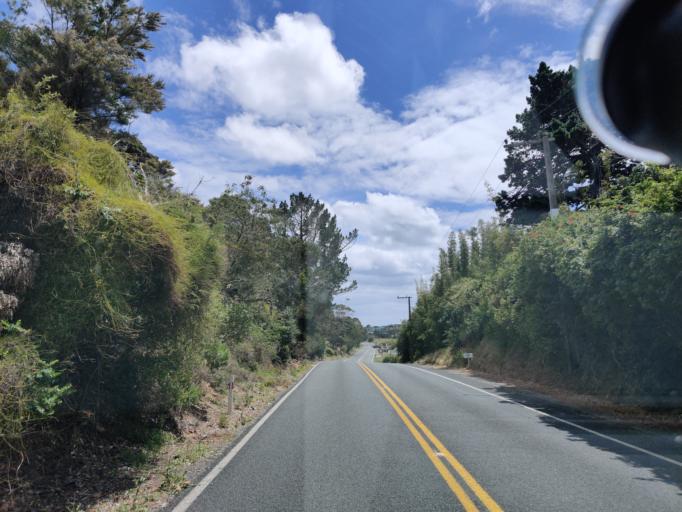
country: NZ
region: Northland
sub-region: Far North District
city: Kaitaia
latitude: -34.8091
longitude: 173.1156
